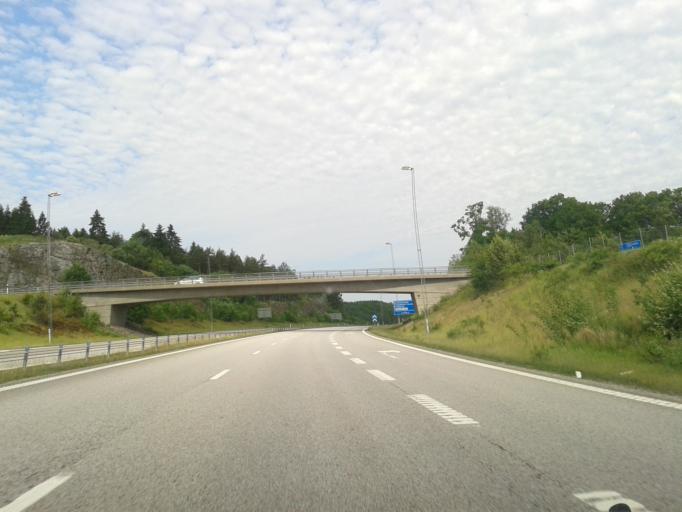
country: SE
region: Vaestra Goetaland
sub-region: Munkedals Kommun
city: Munkedal
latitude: 58.4876
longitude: 11.5888
